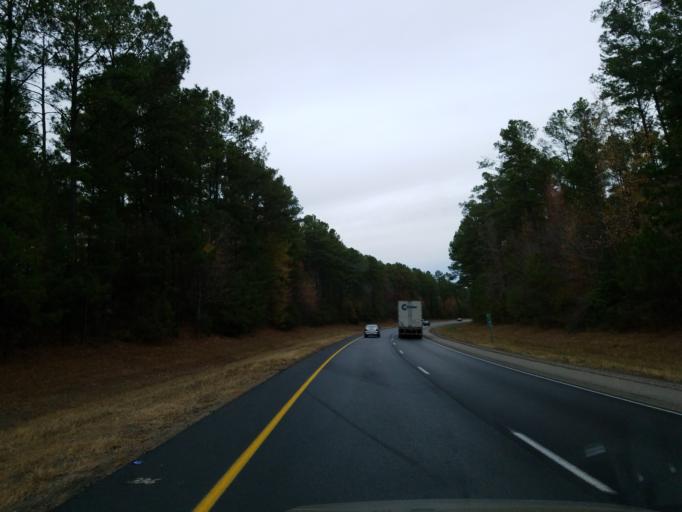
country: US
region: Mississippi
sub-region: Lauderdale County
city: Nellieburg
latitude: 32.3001
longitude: -88.8057
